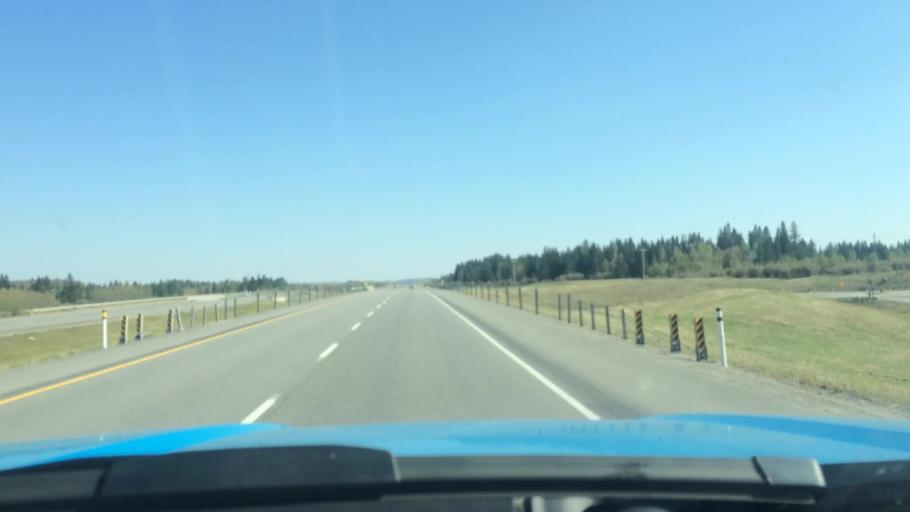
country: CA
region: Alberta
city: Cochrane
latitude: 51.1317
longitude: -114.6958
